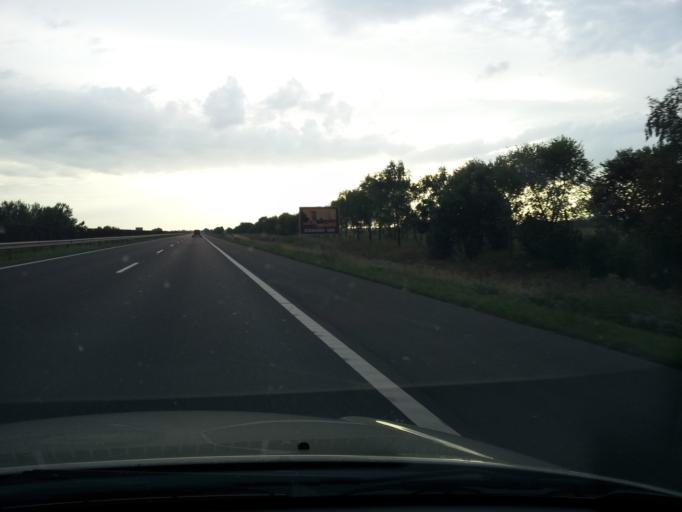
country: HU
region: Heves
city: Karacsond
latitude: 47.7069
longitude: 20.1315
